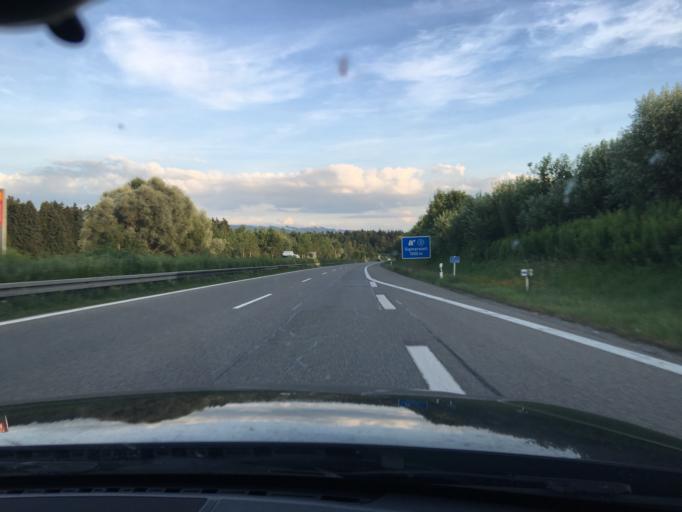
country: DE
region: Bavaria
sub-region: Swabia
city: Weissensberg
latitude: 47.5928
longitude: 9.7346
